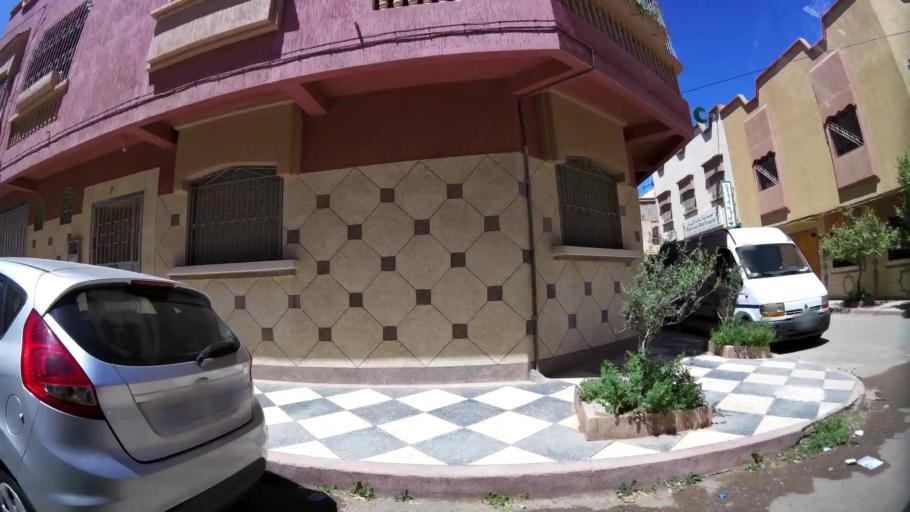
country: MA
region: Oriental
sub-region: Oujda-Angad
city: Oujda
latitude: 34.6587
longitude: -1.9405
